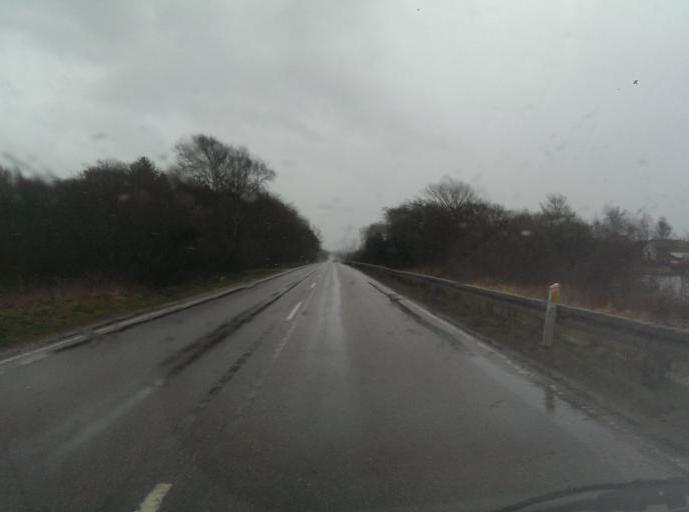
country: DK
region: Central Jutland
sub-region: Ringkobing-Skjern Kommune
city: Skjern
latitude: 55.9746
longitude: 8.4669
